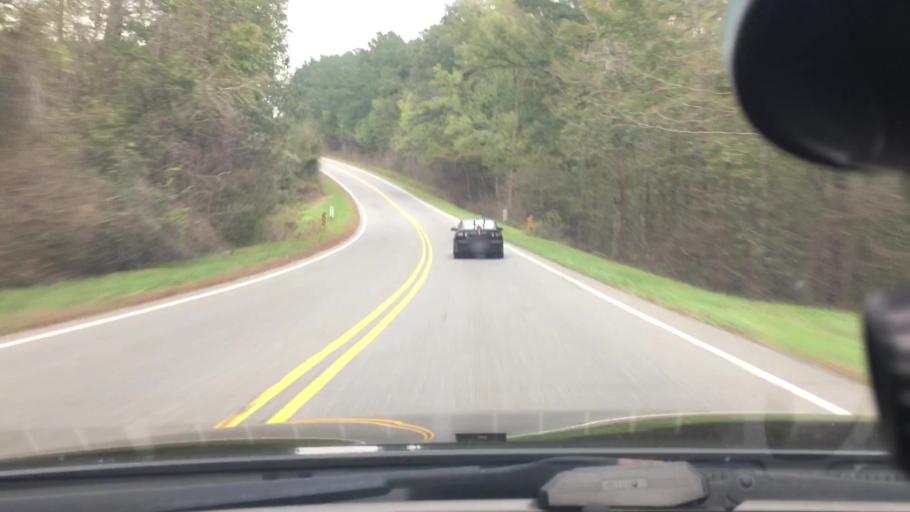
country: US
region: North Carolina
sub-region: Moore County
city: Robbins
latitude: 35.3902
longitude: -79.6413
